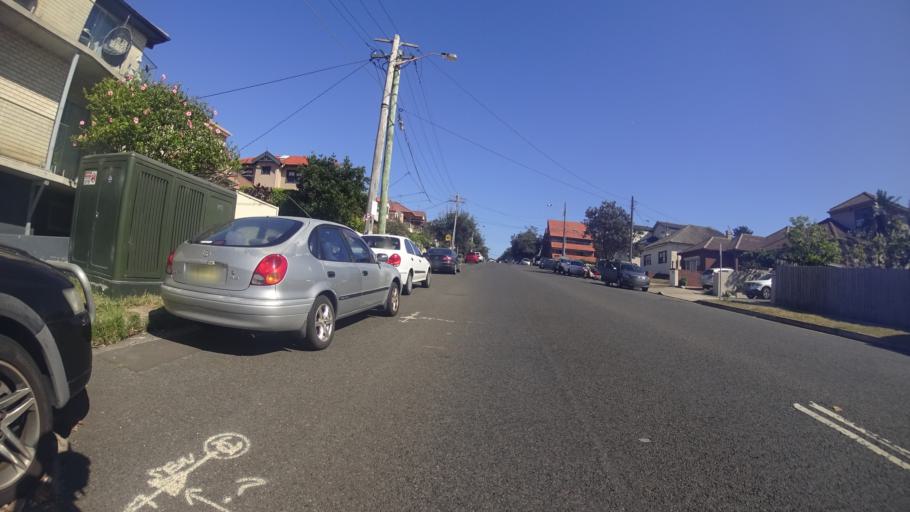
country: AU
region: New South Wales
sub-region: Randwick
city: South Coogee
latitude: -33.9423
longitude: 151.2624
